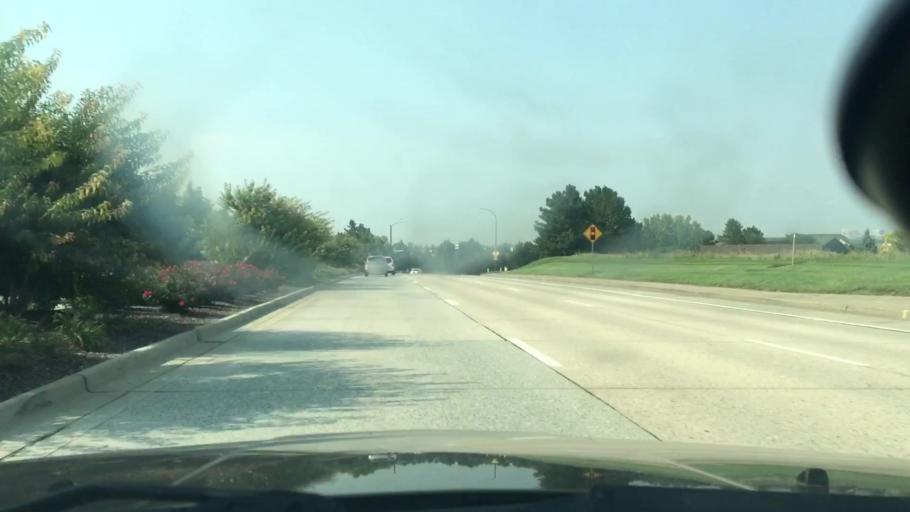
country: US
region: Colorado
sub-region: Douglas County
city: Acres Green
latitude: 39.5532
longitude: -104.9114
